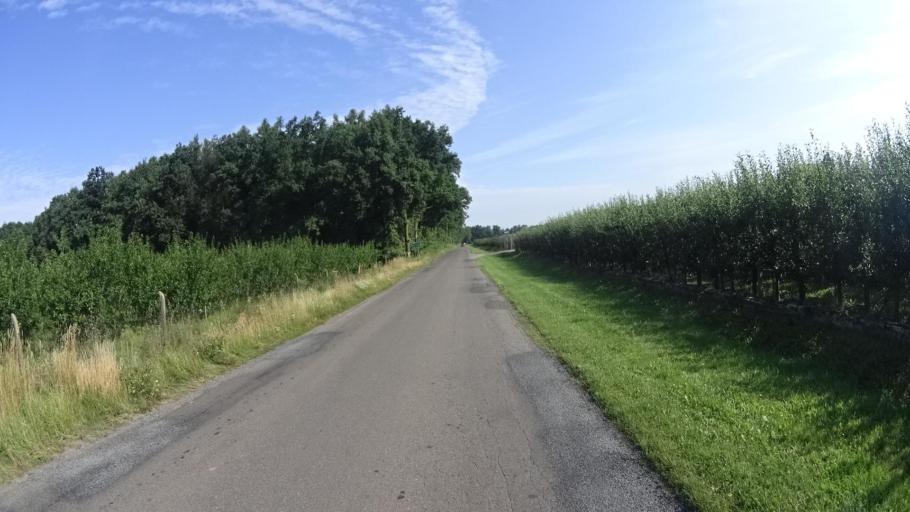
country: PL
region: Masovian Voivodeship
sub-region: Powiat grojecki
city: Goszczyn
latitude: 51.7744
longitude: 20.8537
